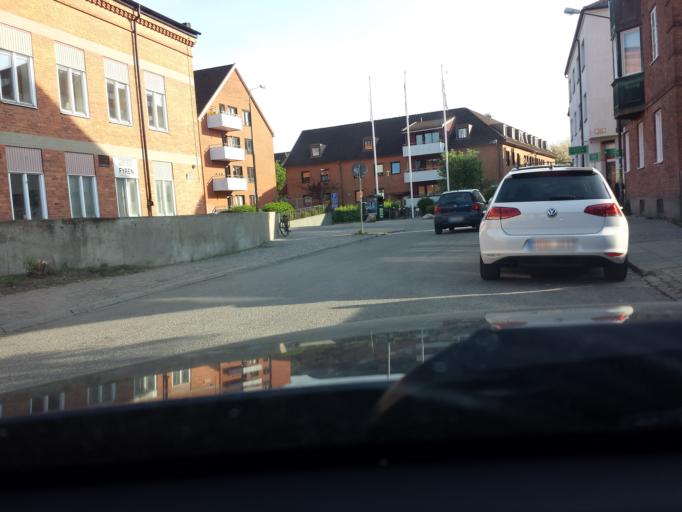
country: SE
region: Skane
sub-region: Malmo
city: Malmoe
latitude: 55.5885
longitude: 13.0159
